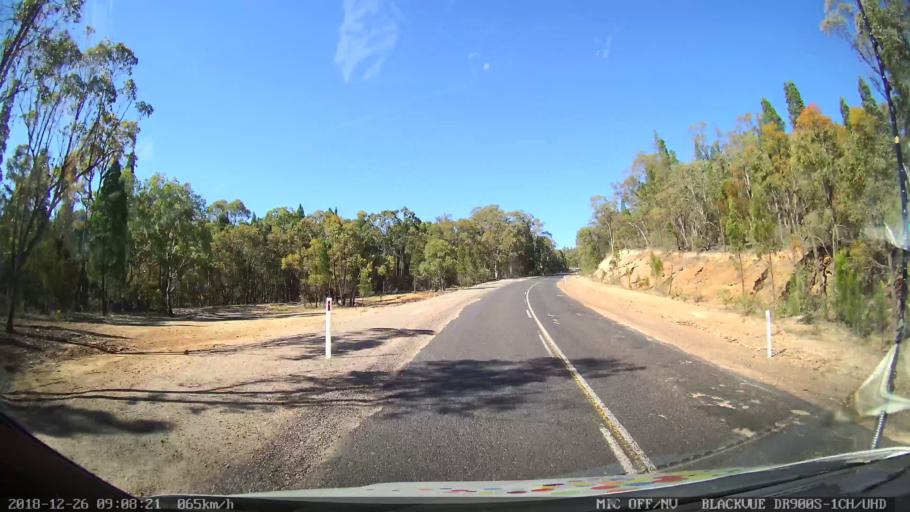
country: AU
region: New South Wales
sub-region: Mid-Western Regional
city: Kandos
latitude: -32.7155
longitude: 150.0028
